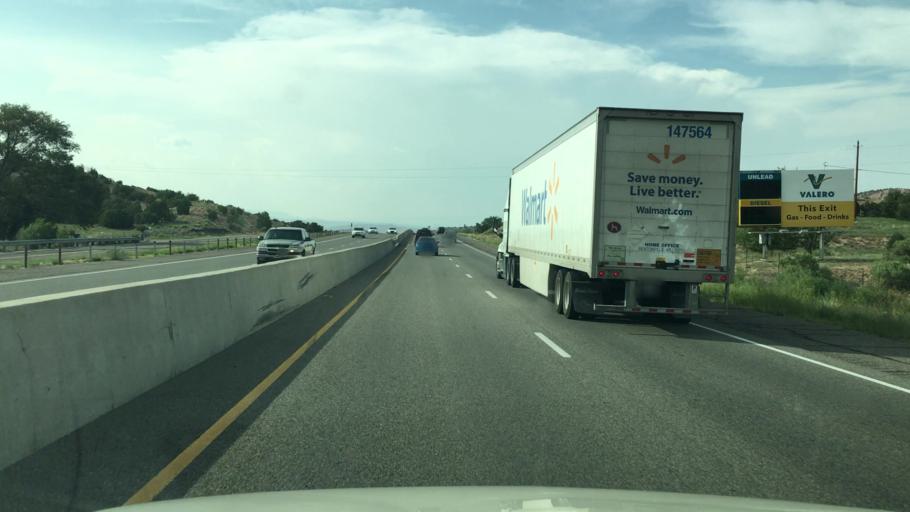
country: US
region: New Mexico
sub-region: Santa Fe County
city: Nambe
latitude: 35.8101
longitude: -105.9671
